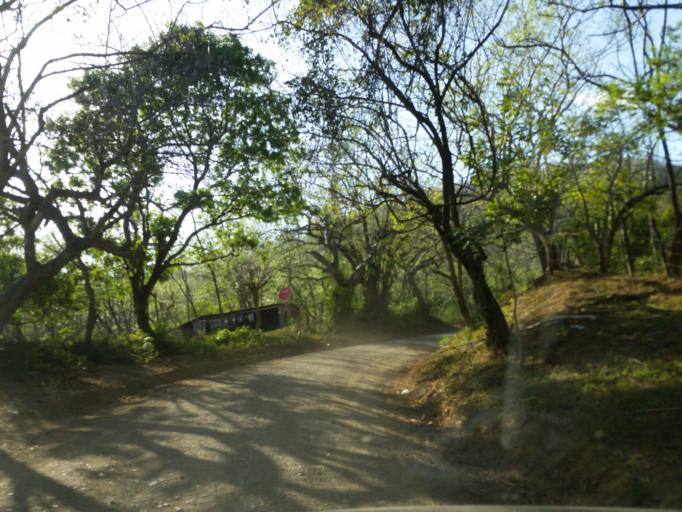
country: NI
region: Rivas
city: San Juan del Sur
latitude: 11.2185
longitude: -85.8131
